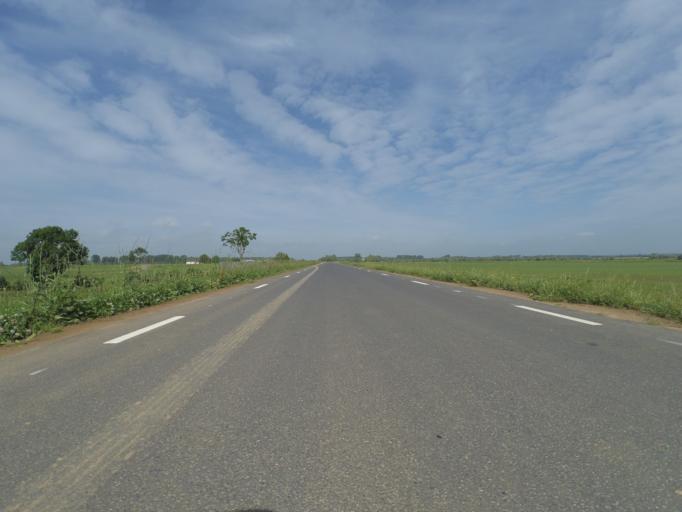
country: NL
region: Utrecht
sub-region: Gemeente Wijk bij Duurstede
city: Wijk bij Duurstede
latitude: 51.9648
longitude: 5.3843
